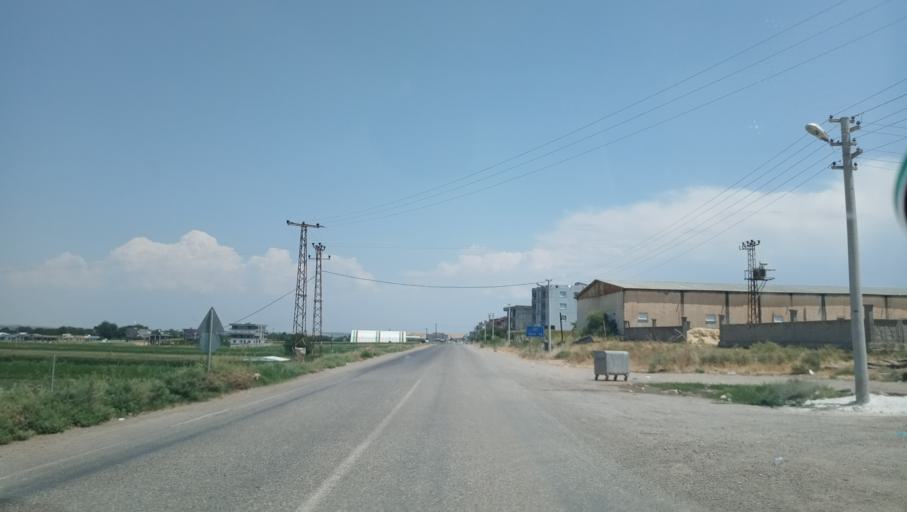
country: TR
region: Diyarbakir
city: Aralik
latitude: 37.8291
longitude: 40.6686
